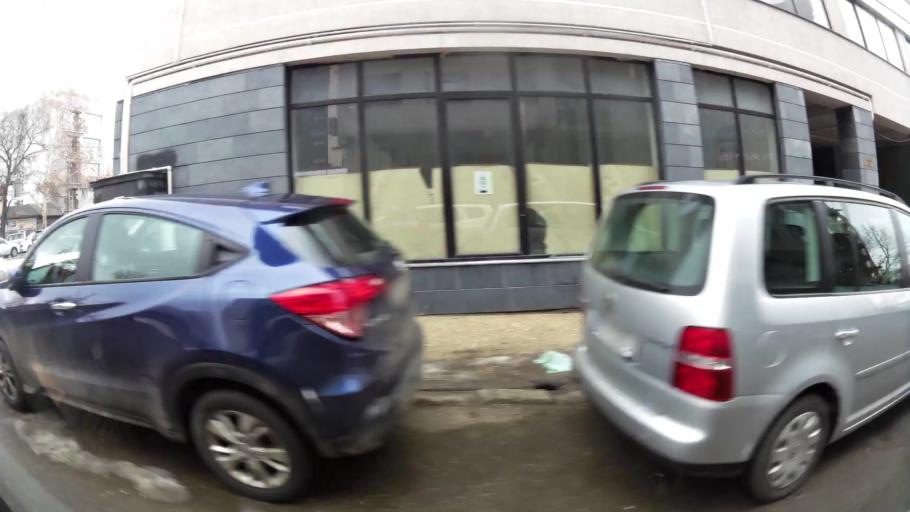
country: RO
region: Bucuresti
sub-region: Municipiul Bucuresti
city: Bucharest
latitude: 44.4222
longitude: 26.1296
